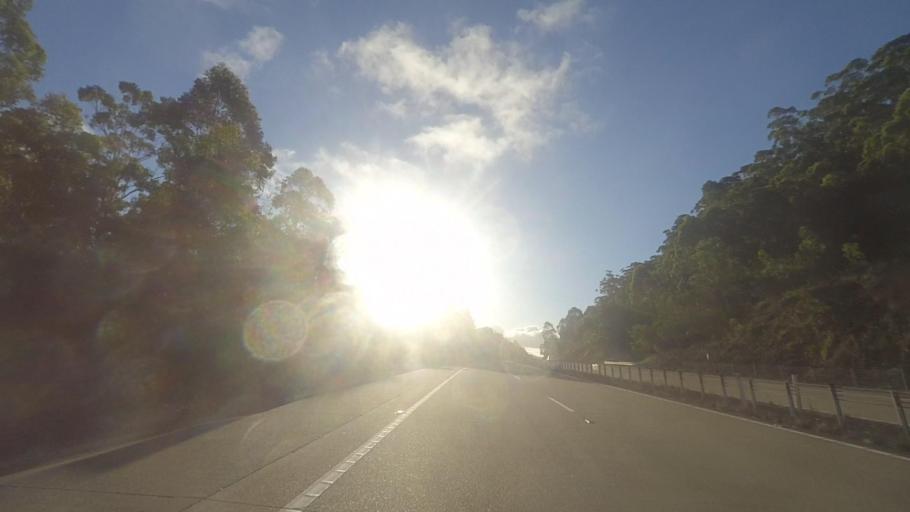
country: AU
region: New South Wales
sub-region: Great Lakes
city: Bulahdelah
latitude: -32.3879
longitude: 152.2538
